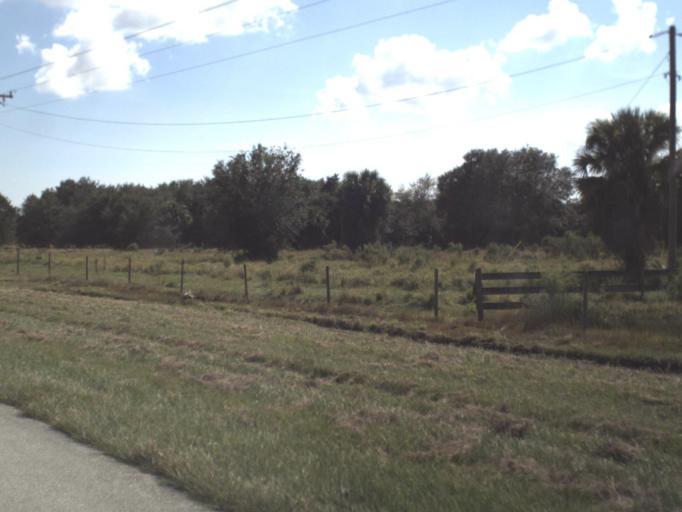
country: US
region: Florida
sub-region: Okeechobee County
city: Okeechobee
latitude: 27.3205
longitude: -80.9160
